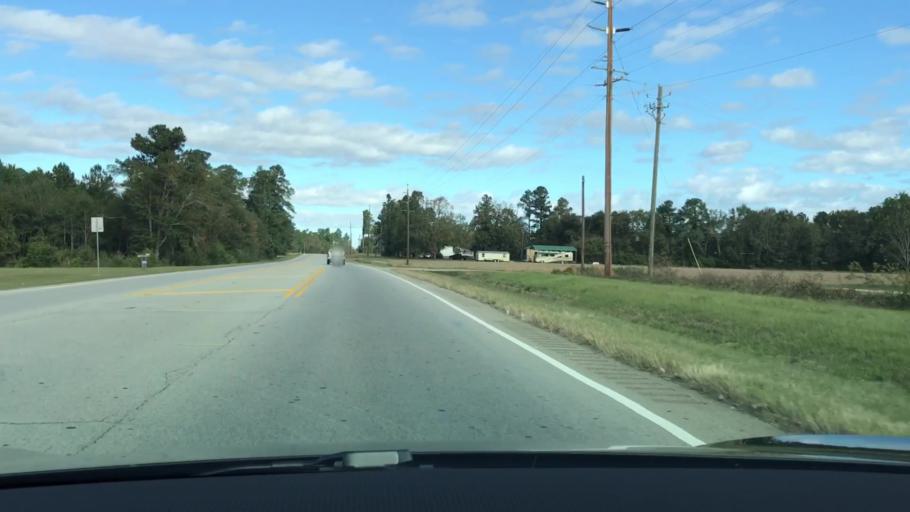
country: US
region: Georgia
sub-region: Jefferson County
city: Louisville
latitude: 33.0307
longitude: -82.4049
